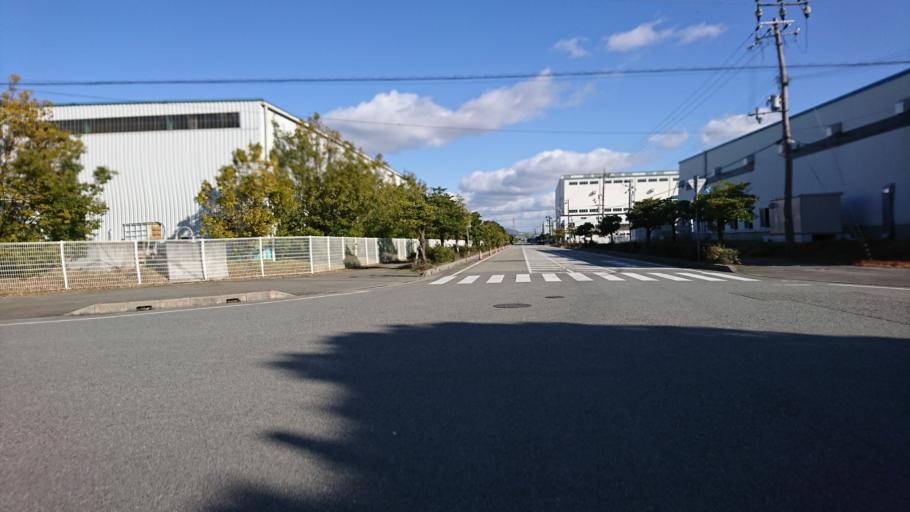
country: JP
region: Hyogo
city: Kakogawacho-honmachi
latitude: 34.7515
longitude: 134.7830
